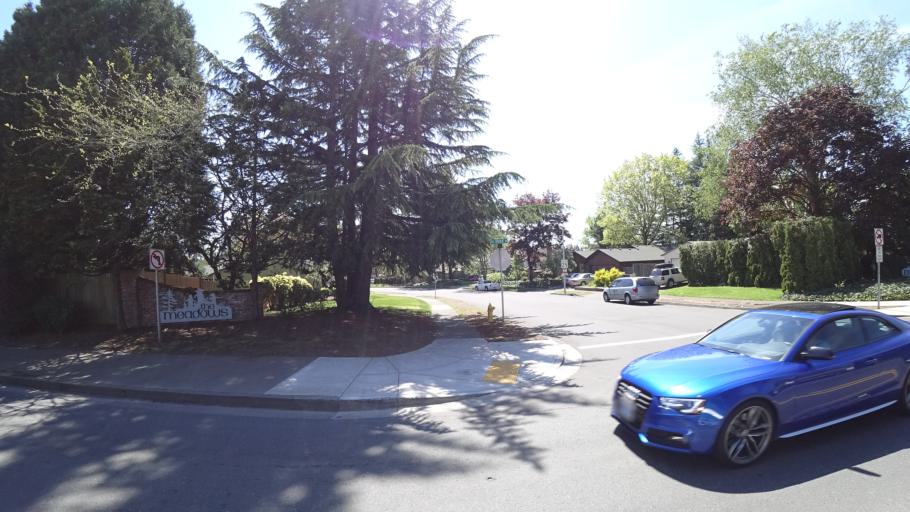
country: US
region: Oregon
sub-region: Washington County
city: Hillsboro
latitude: 45.5032
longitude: -122.9600
